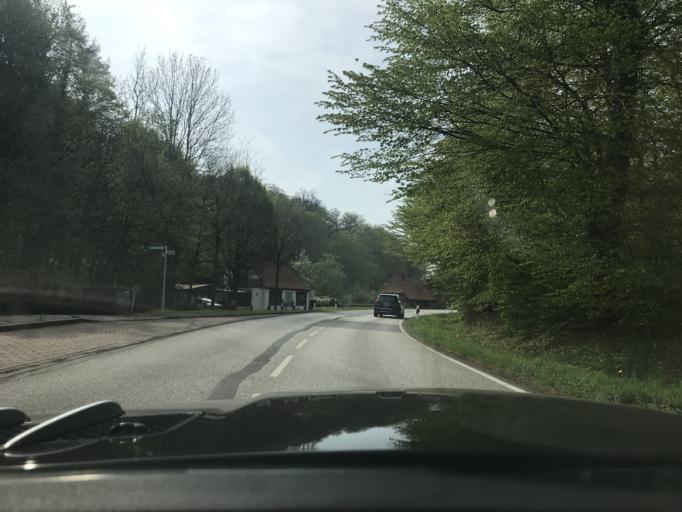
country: DE
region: Schleswig-Holstein
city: Gromitz
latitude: 54.1859
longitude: 10.9813
